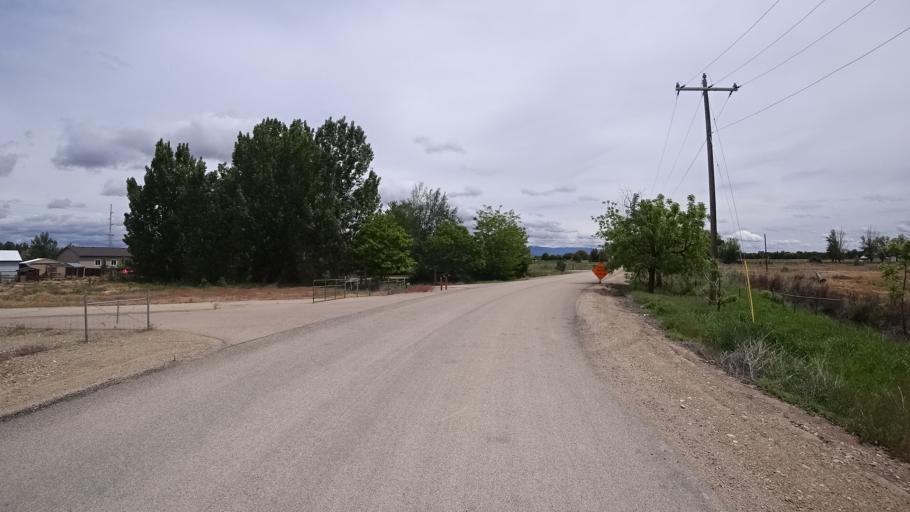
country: US
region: Idaho
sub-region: Ada County
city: Star
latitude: 43.6901
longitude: -116.4582
